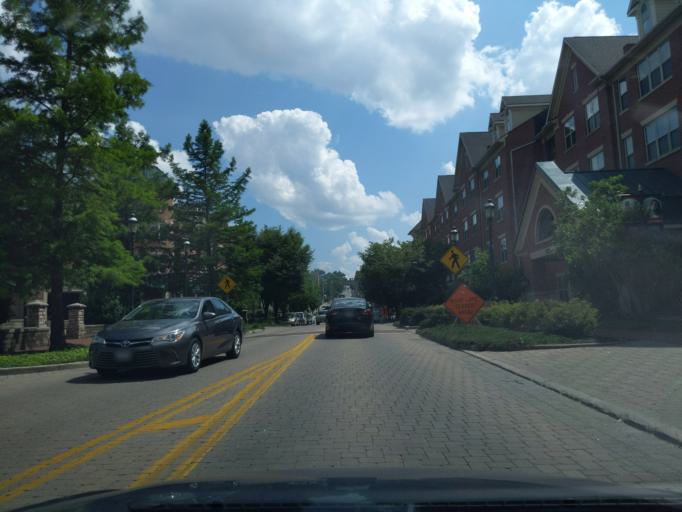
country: US
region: Ohio
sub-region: Hamilton County
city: Saint Bernard
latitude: 39.1349
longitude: -84.5057
